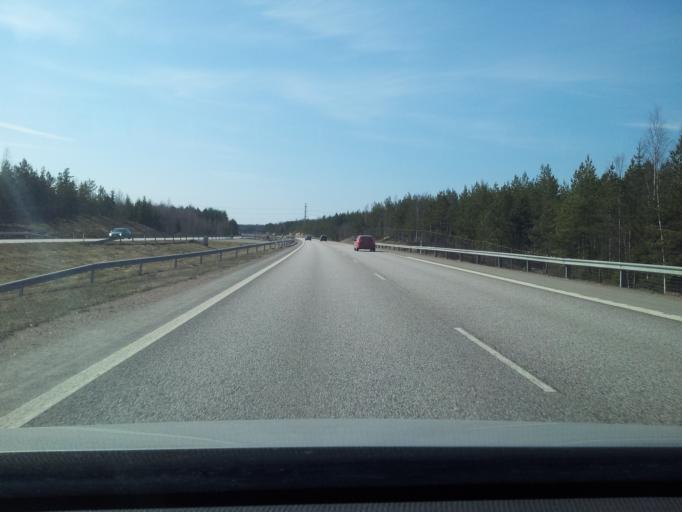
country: FI
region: Kymenlaakso
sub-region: Kotka-Hamina
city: Hamina
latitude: 60.5693
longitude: 27.0644
